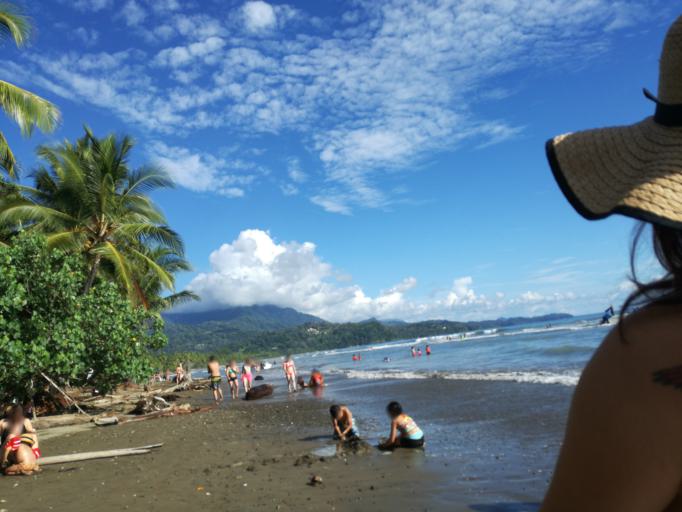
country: CR
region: San Jose
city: Daniel Flores
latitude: 9.1539
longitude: -83.7513
